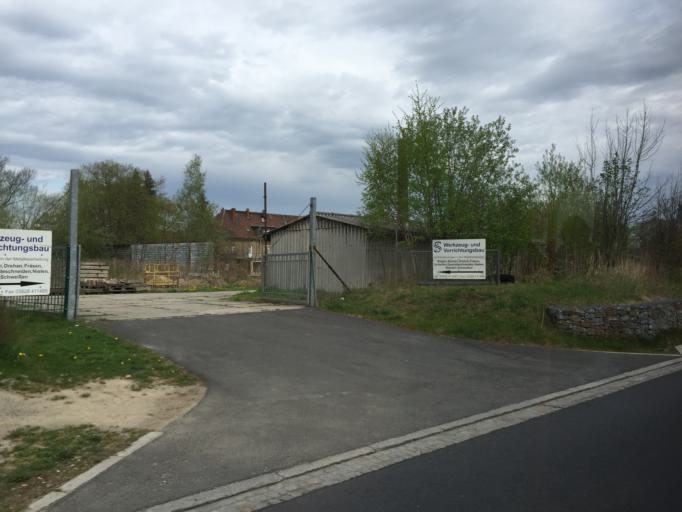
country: DE
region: Saxony
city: Radeberg
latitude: 51.1124
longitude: 13.9186
